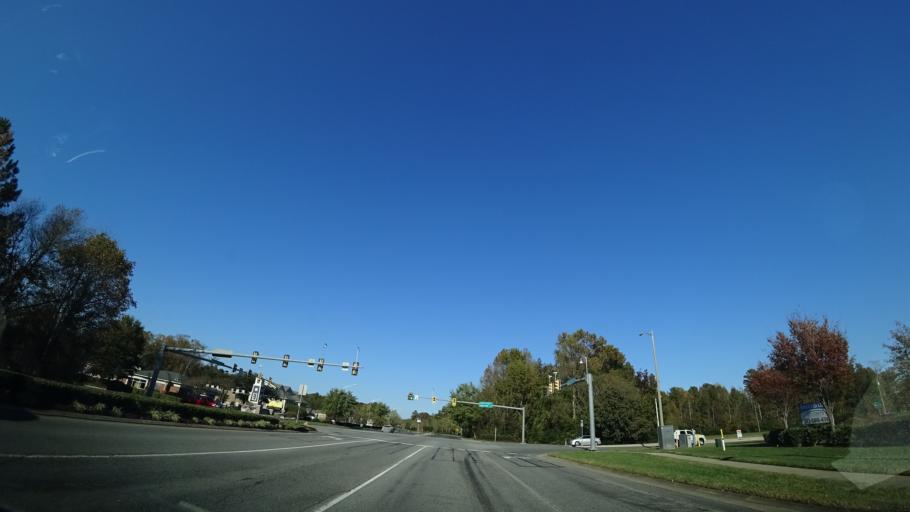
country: US
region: Virginia
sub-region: City of Portsmouth
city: Portsmouth Heights
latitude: 36.8760
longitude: -76.4384
